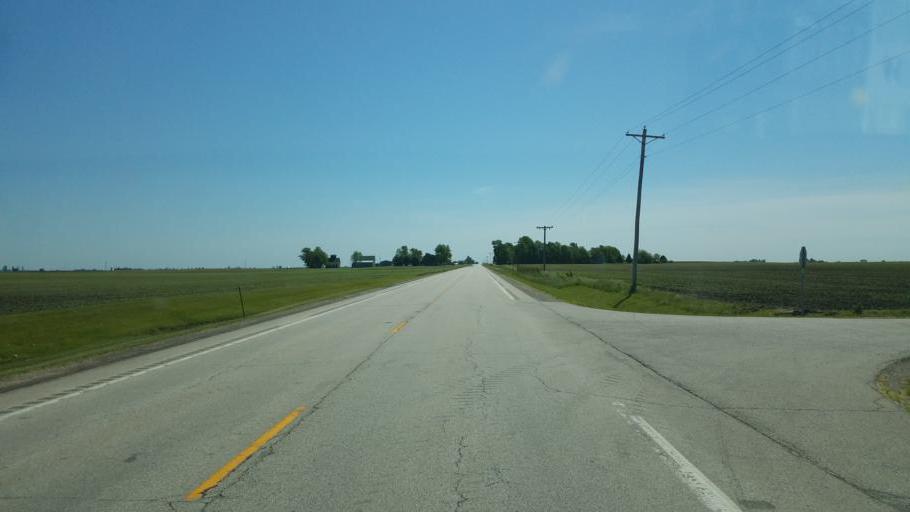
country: US
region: Illinois
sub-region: McLean County
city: Heyworth
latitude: 40.3123
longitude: -88.9207
